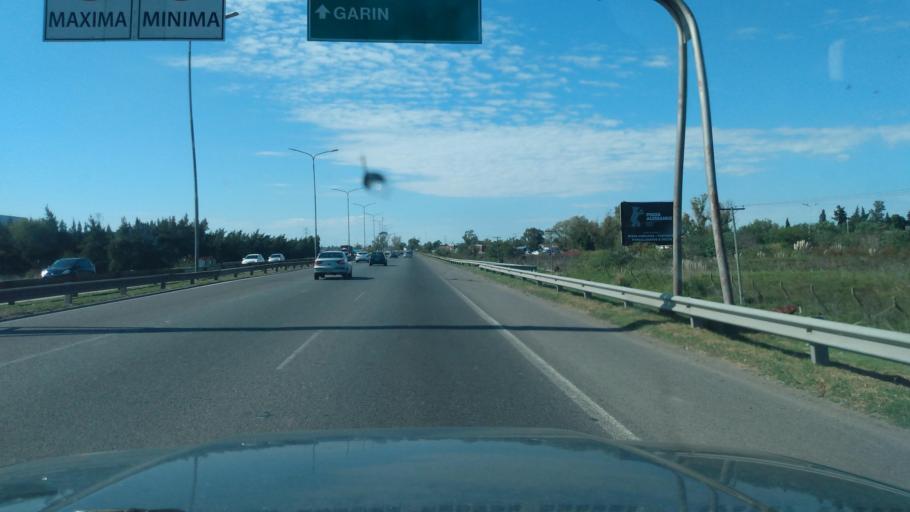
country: AR
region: Buenos Aires
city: Hurlingham
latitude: -34.5519
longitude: -58.6171
